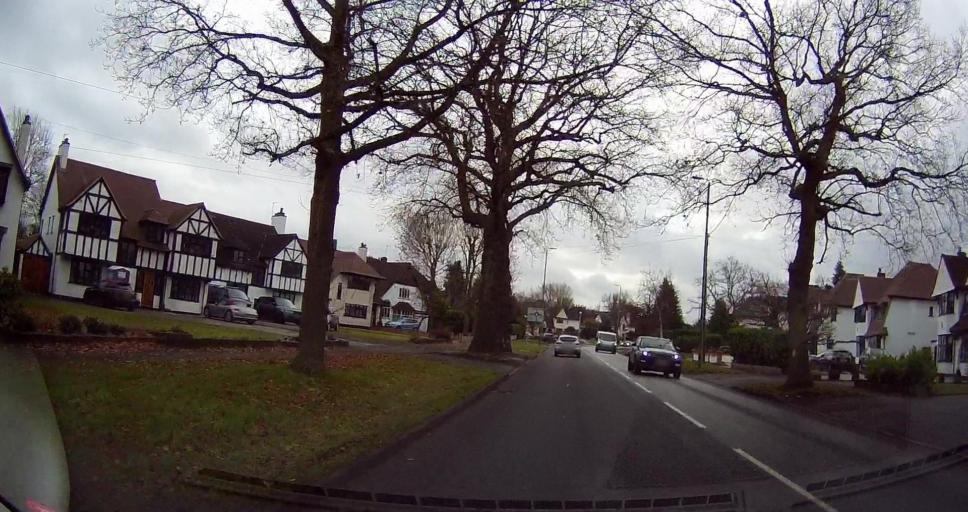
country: GB
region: England
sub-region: Greater London
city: Orpington
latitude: 51.3924
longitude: 0.0900
